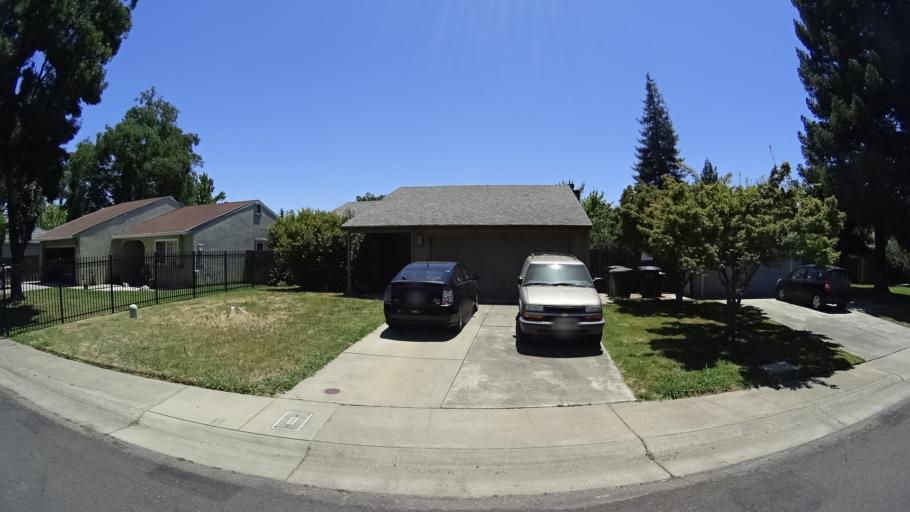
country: US
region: California
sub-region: Sacramento County
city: Sacramento
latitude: 38.5377
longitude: -121.4802
